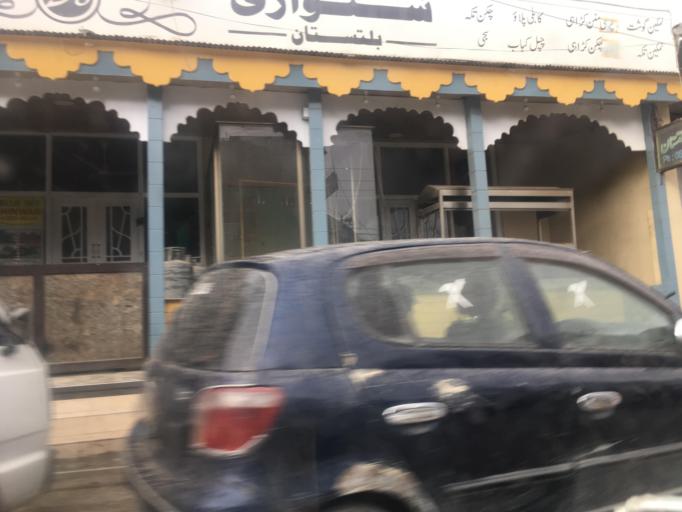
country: PK
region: Gilgit-Baltistan
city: Skardu
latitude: 35.3013
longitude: 75.6292
